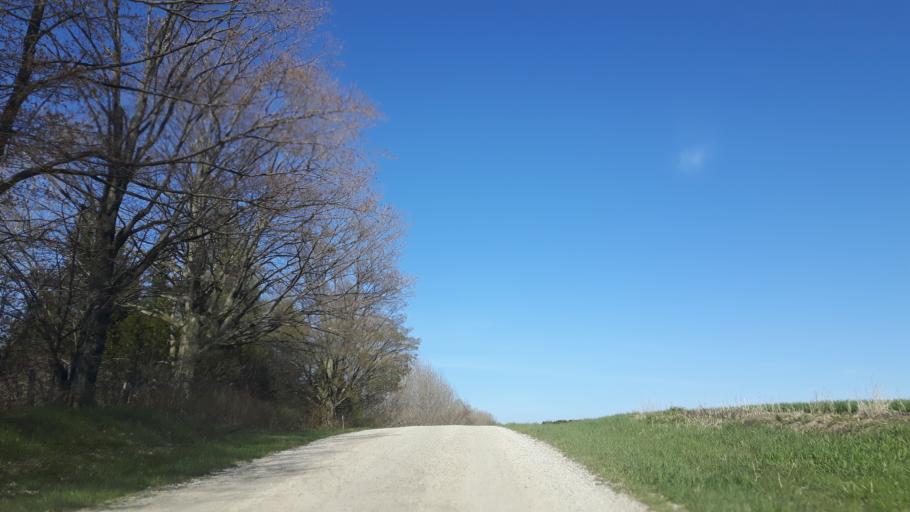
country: CA
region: Ontario
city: Goderich
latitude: 43.6613
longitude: -81.6749
